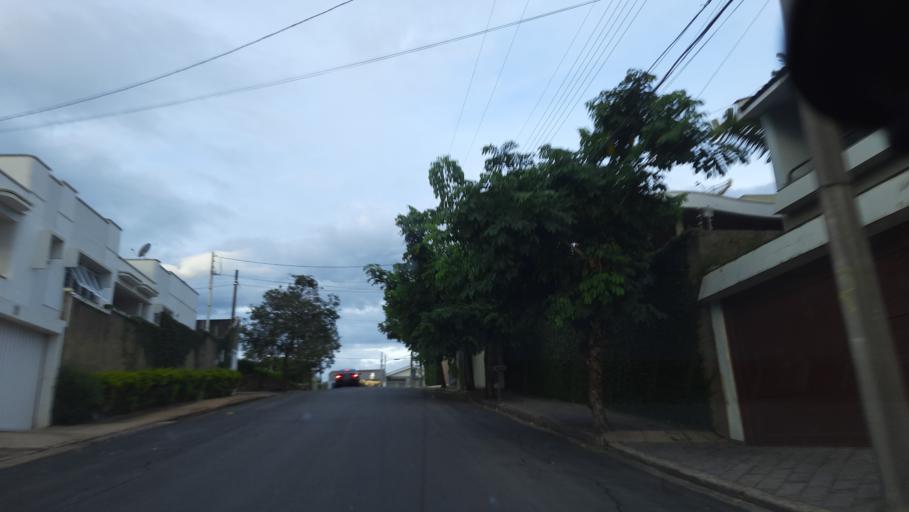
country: BR
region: Sao Paulo
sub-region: Sao Joao Da Boa Vista
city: Sao Joao da Boa Vista
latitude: -21.9660
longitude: -46.7920
